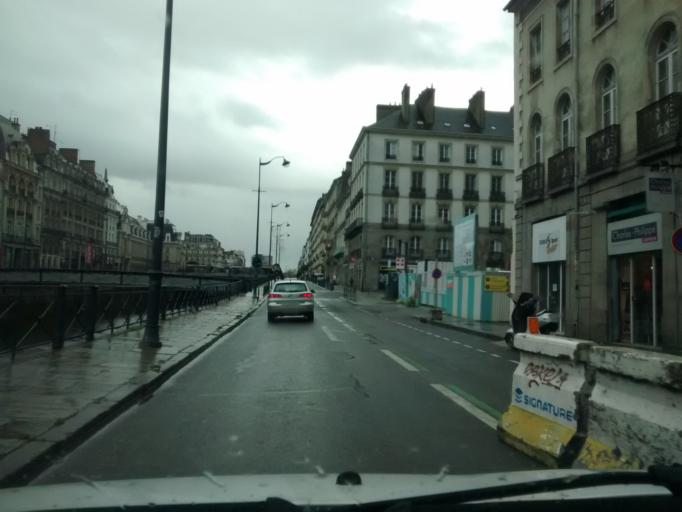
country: FR
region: Brittany
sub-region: Departement d'Ille-et-Vilaine
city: Rennes
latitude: 48.1102
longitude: -1.6757
